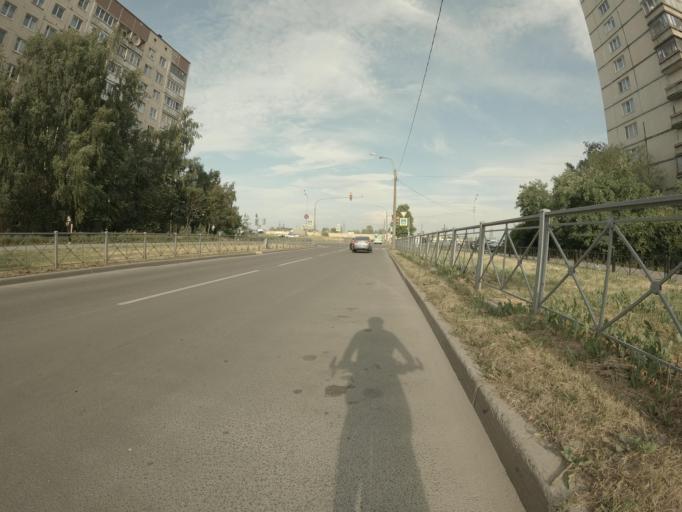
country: RU
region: St.-Petersburg
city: Krasnogvargeisky
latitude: 59.9396
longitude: 30.5005
